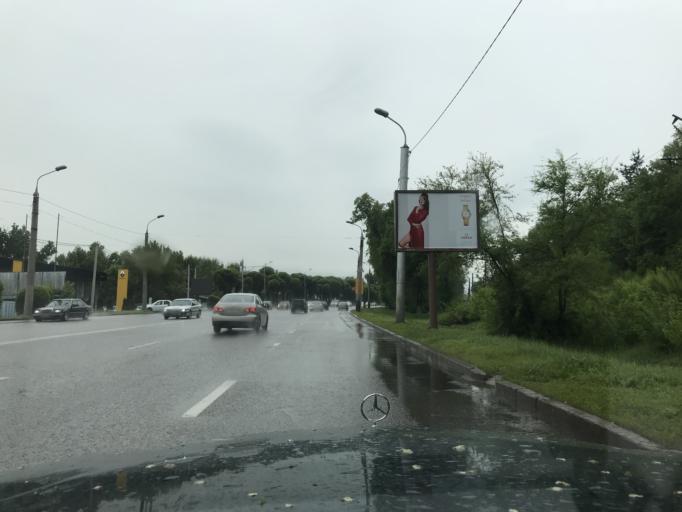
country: KZ
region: Almaty Qalasy
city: Almaty
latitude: 43.3048
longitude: 76.9530
